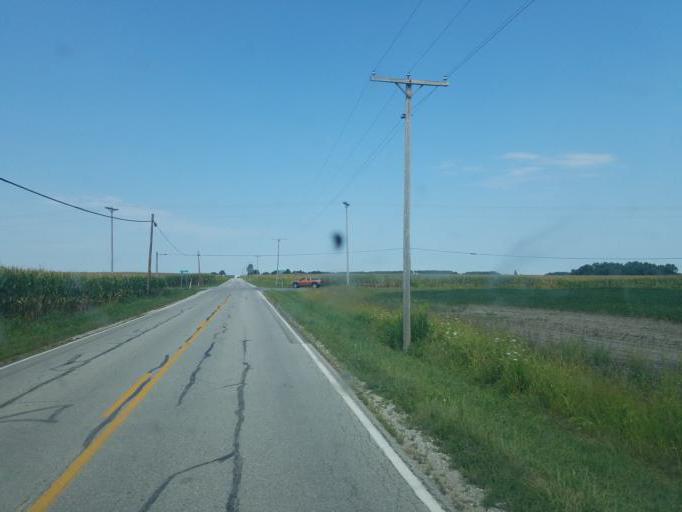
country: US
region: Ohio
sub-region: Marion County
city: Marion
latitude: 40.6580
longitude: -83.2244
